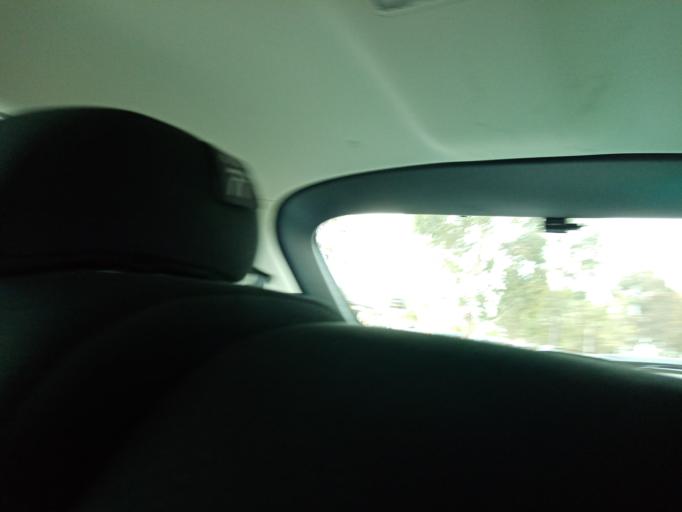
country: AU
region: Western Australia
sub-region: City of Cockburn
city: Success
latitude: -32.1319
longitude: 115.8542
